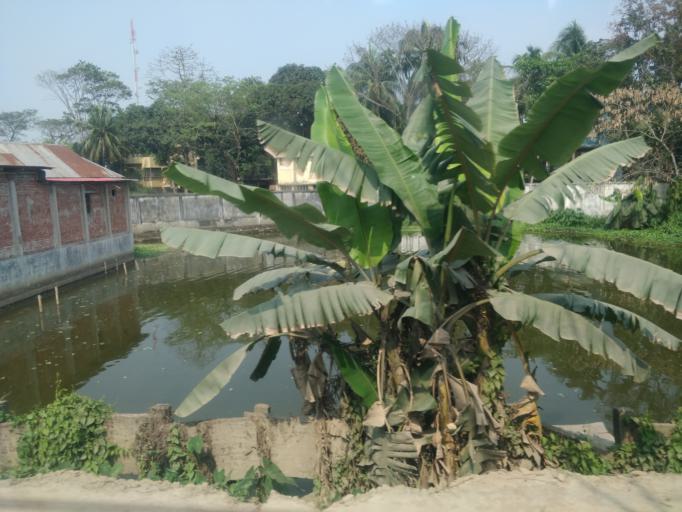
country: BD
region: Sylhet
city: Habiganj
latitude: 24.3637
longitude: 91.4192
